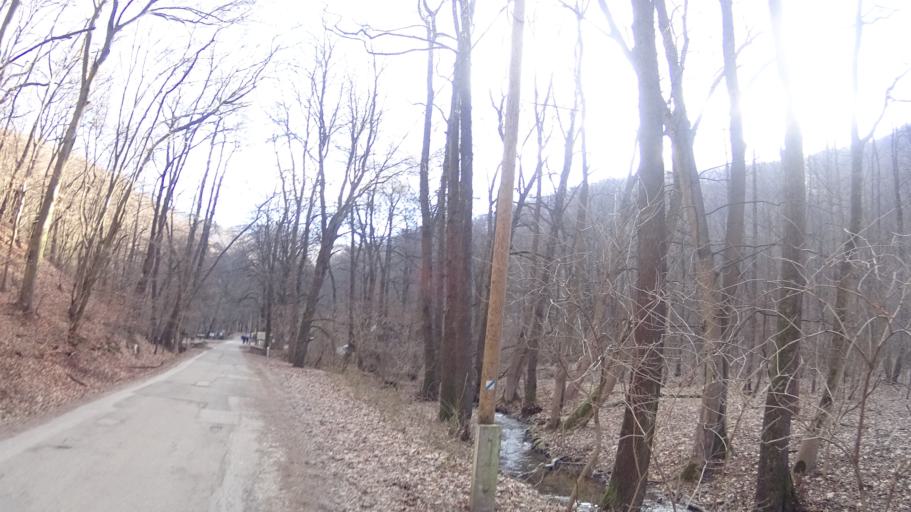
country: HU
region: Heves
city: Szilvasvarad
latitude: 48.0904
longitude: 20.4013
